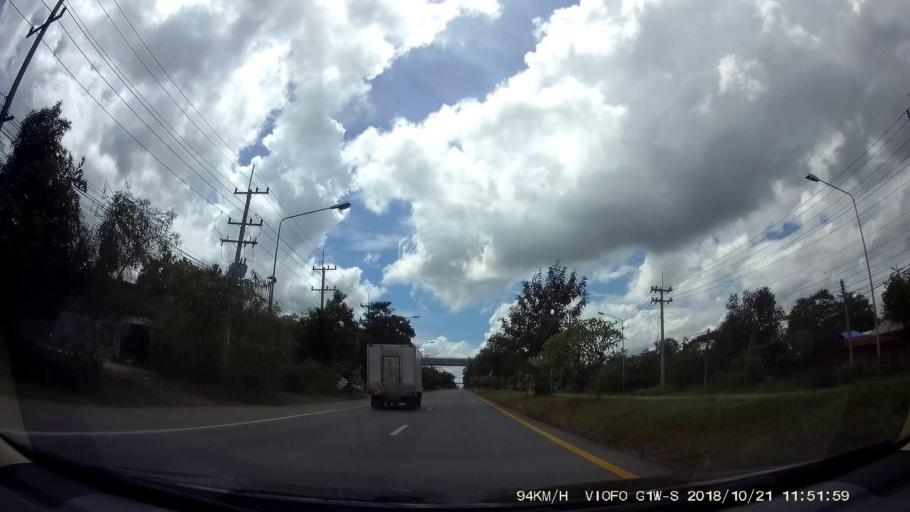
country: TH
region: Chaiyaphum
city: Chatturat
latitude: 15.6158
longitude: 101.9143
